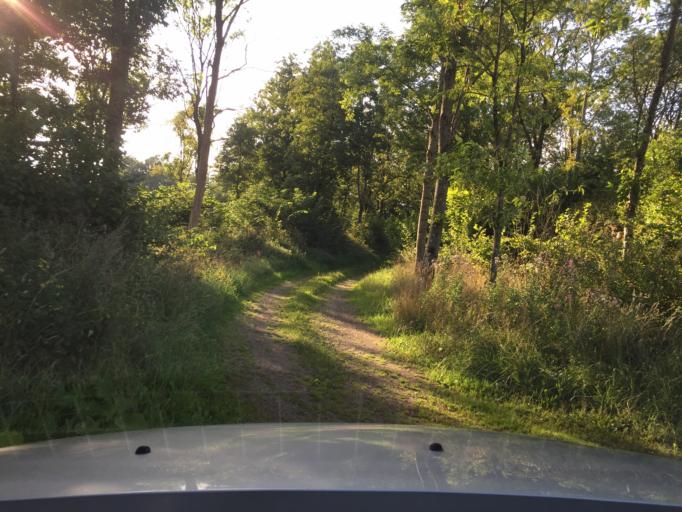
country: SE
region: Skane
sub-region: Hassleholms Kommun
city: Sosdala
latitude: 56.0259
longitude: 13.7037
